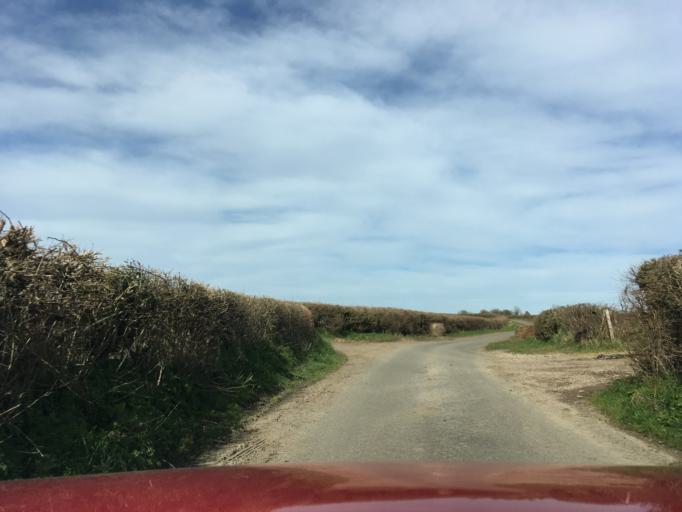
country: GB
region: England
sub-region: Wiltshire
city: Luckington
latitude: 51.5398
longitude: -2.2389
